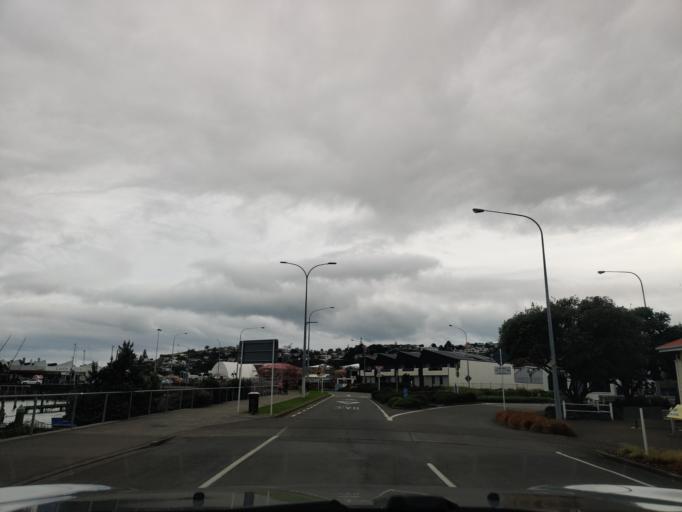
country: NZ
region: Hawke's Bay
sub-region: Napier City
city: Napier
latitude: -39.4819
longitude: 176.8960
